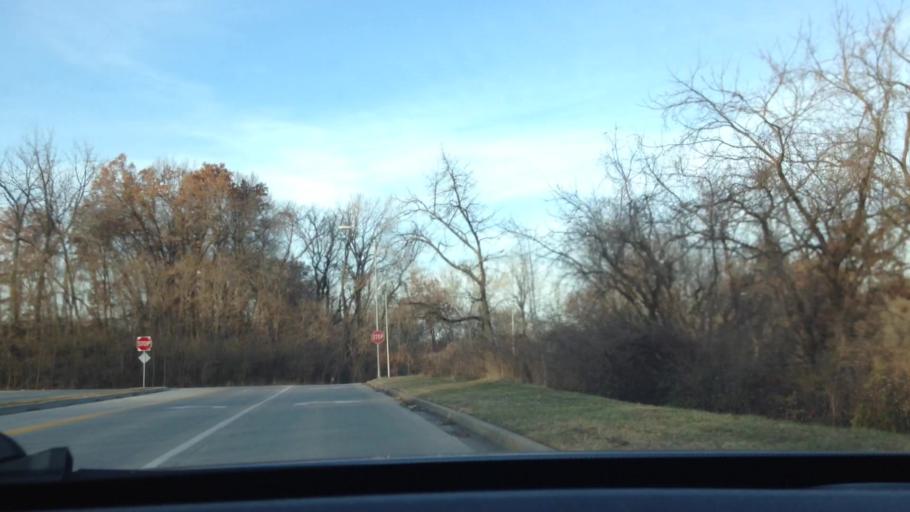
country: US
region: Missouri
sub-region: Clay County
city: Claycomo
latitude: 39.1669
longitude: -94.5148
